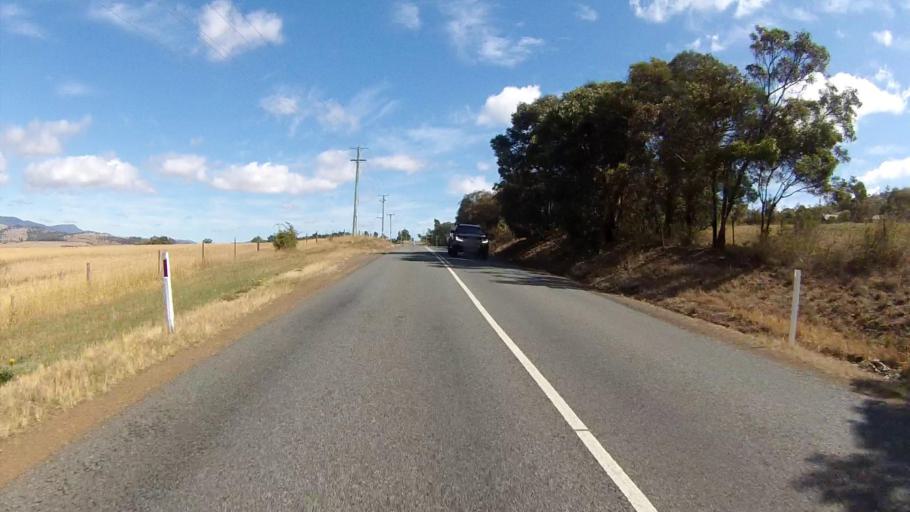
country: AU
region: Tasmania
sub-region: Brighton
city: Bridgewater
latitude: -42.7194
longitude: 147.2784
